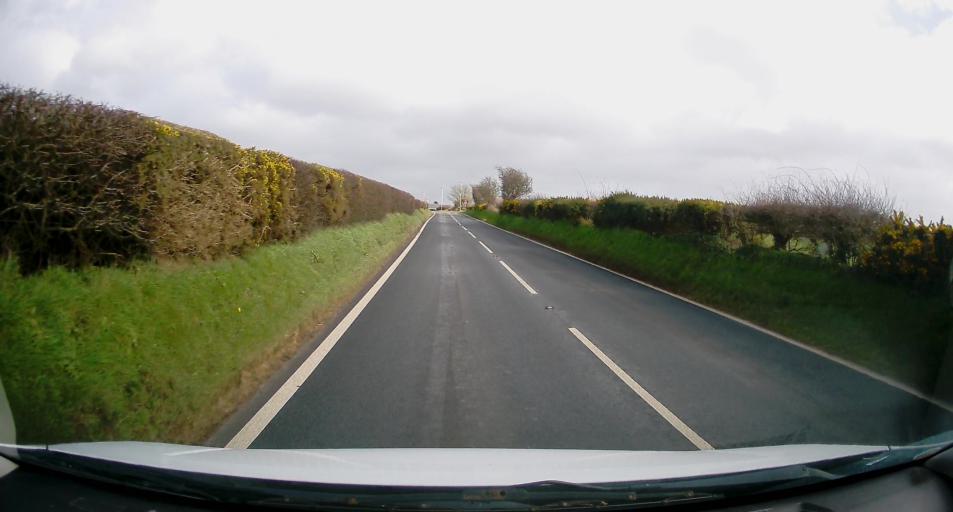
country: GB
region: Wales
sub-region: County of Ceredigion
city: Aberporth
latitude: 52.1101
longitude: -4.5438
